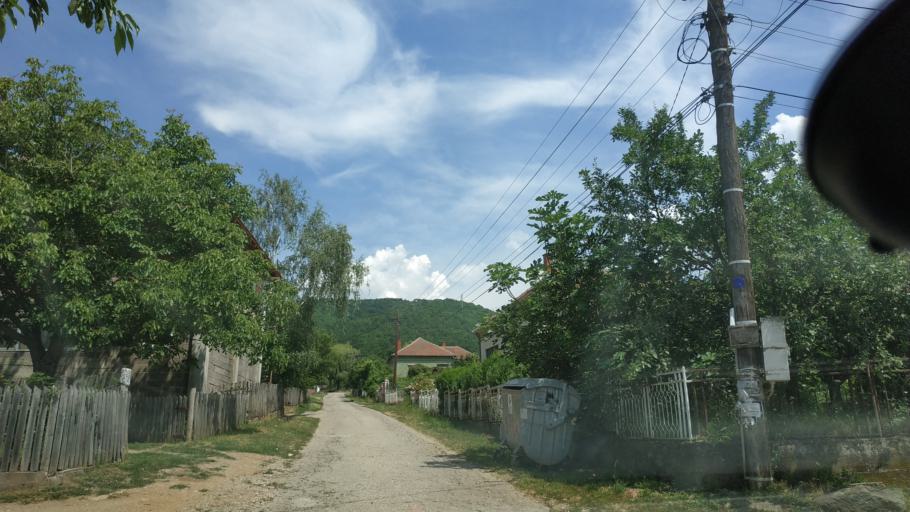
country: RS
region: Central Serbia
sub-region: Nisavski Okrug
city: Aleksinac
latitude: 43.5987
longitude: 21.6956
